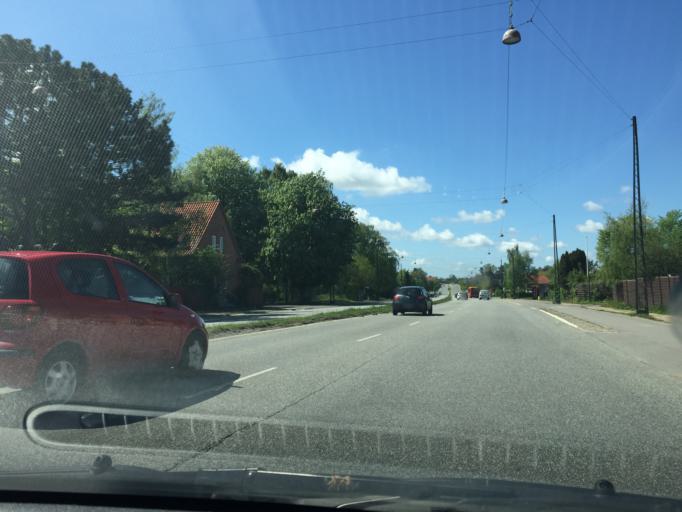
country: DK
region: Capital Region
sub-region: Kobenhavn
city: Vanlose
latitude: 55.6911
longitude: 12.4732
